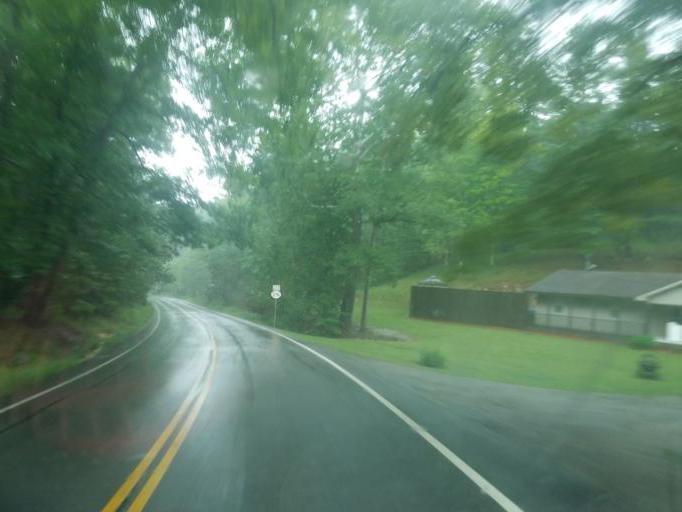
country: US
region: Kentucky
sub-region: Rowan County
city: Morehead
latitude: 38.2722
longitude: -83.3176
